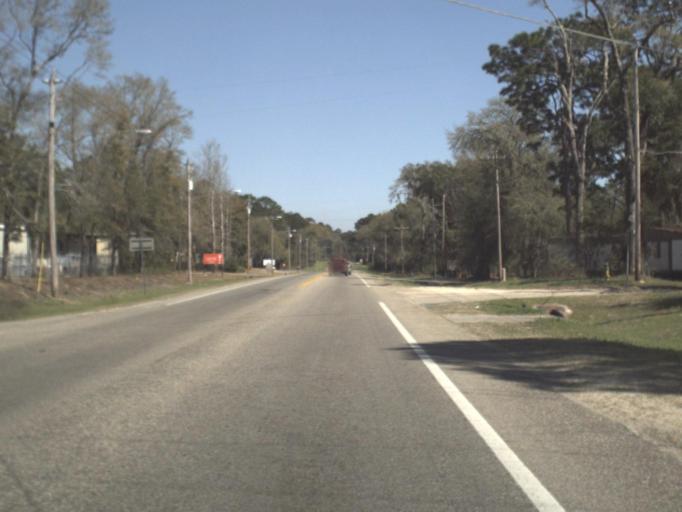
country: US
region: Florida
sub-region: Leon County
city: Tallahassee
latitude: 30.4142
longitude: -84.3403
